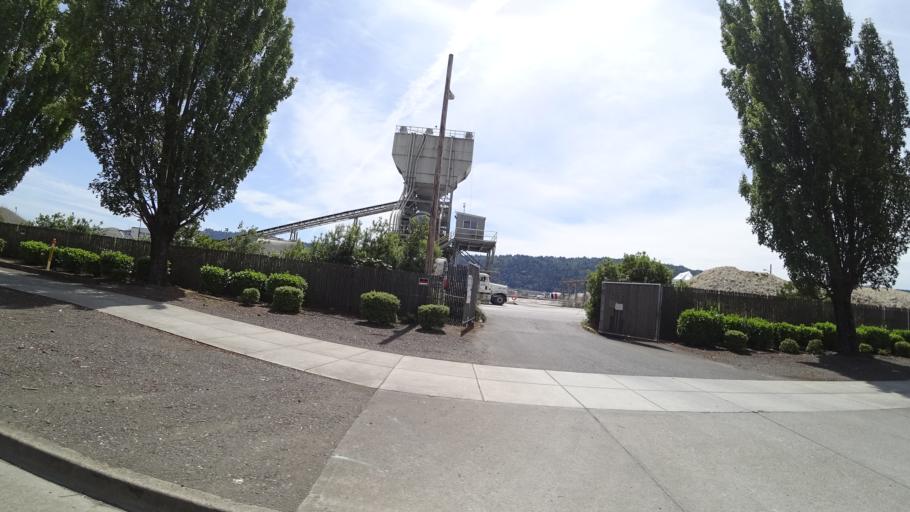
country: US
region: Oregon
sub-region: Multnomah County
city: Portland
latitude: 45.5616
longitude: -122.7142
